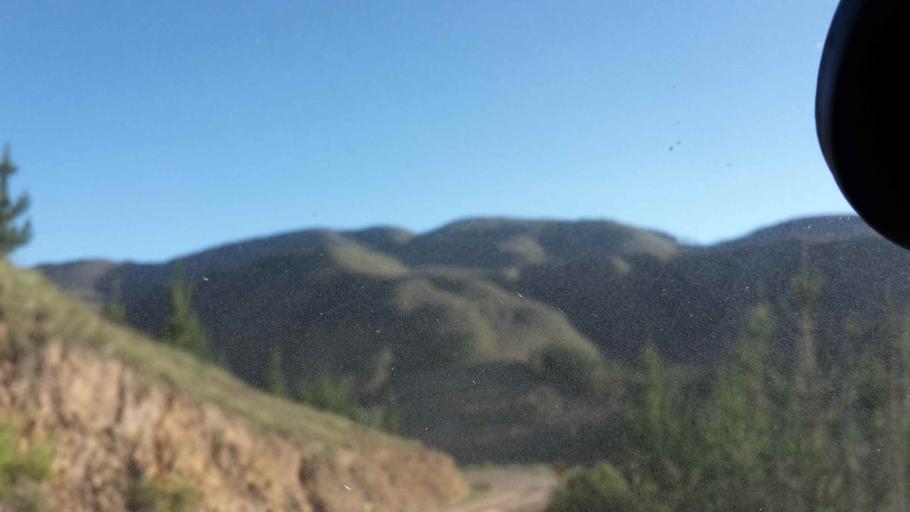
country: BO
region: Cochabamba
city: Arani
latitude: -17.7941
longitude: -65.6004
